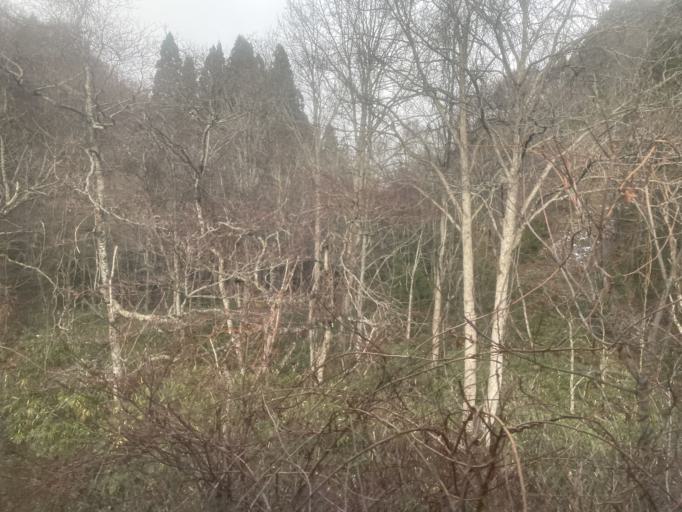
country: JP
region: Aomori
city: Goshogawara
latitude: 41.0772
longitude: 140.5383
